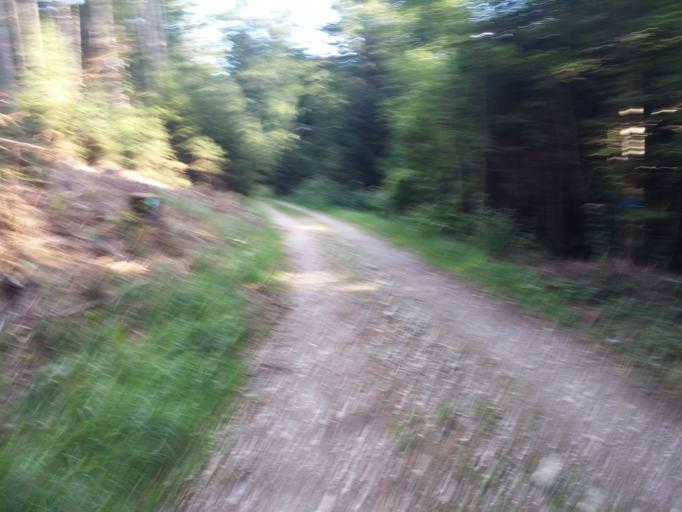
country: DE
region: Bavaria
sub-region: Swabia
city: Woringen
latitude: 47.8782
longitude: 10.2062
